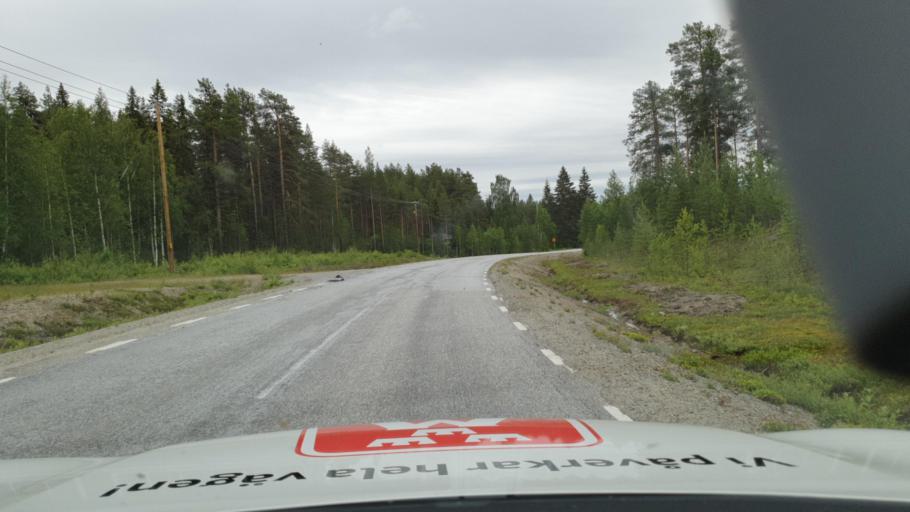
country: SE
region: Vaesterbotten
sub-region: Lycksele Kommun
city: Lycksele
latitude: 64.0866
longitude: 18.3957
